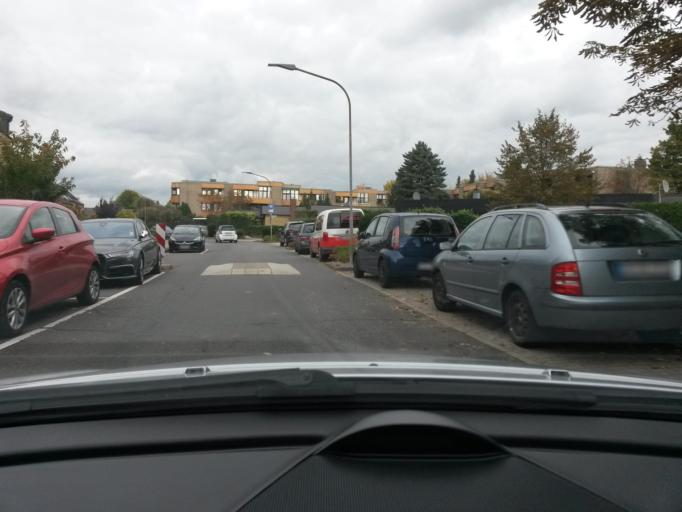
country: DE
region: Schleswig-Holstein
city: Barsbuettel
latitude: 53.5672
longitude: 10.1747
